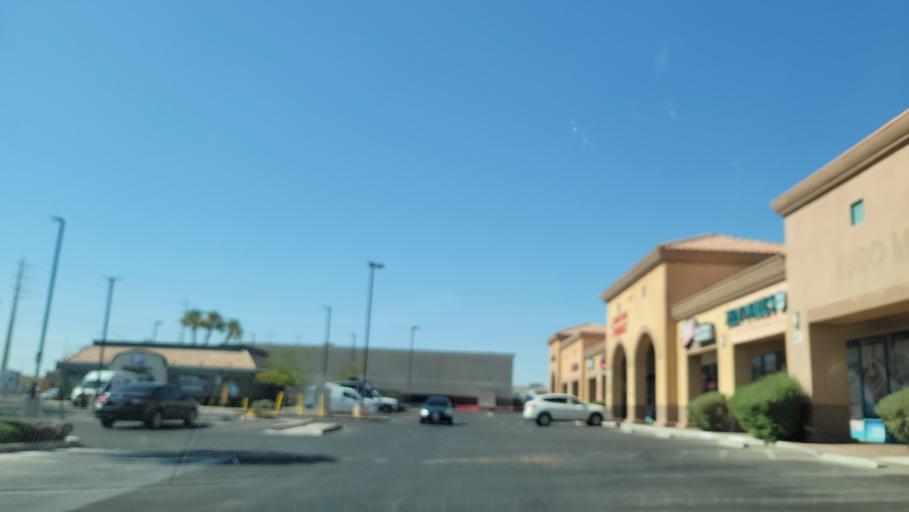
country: US
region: Nevada
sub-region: Clark County
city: Spring Valley
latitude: 36.0868
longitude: -115.2436
